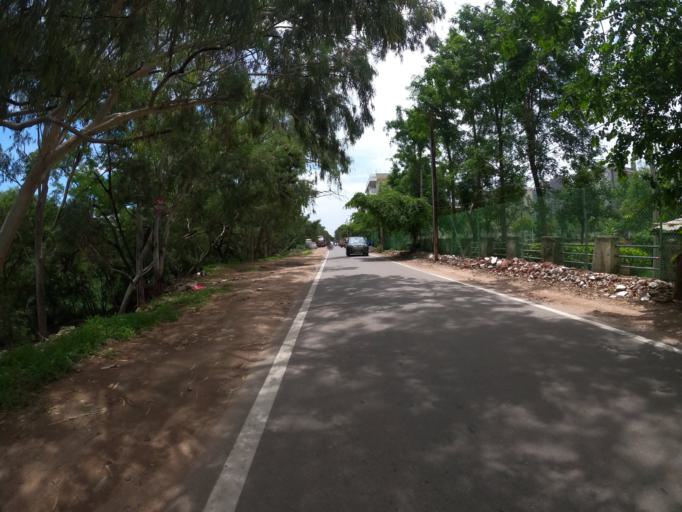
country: IN
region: Telangana
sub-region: Hyderabad
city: Hyderabad
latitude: 17.3711
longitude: 78.4233
